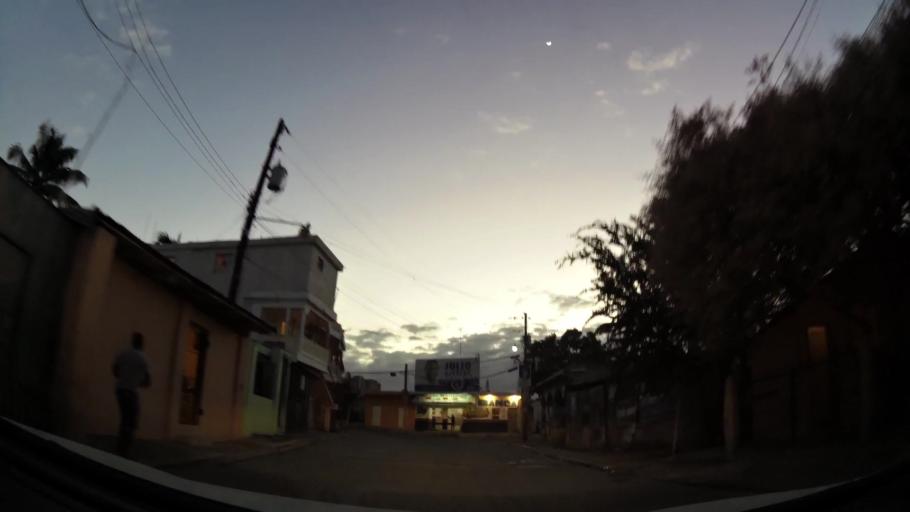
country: DO
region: Nacional
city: La Agustina
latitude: 18.5441
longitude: -69.9397
